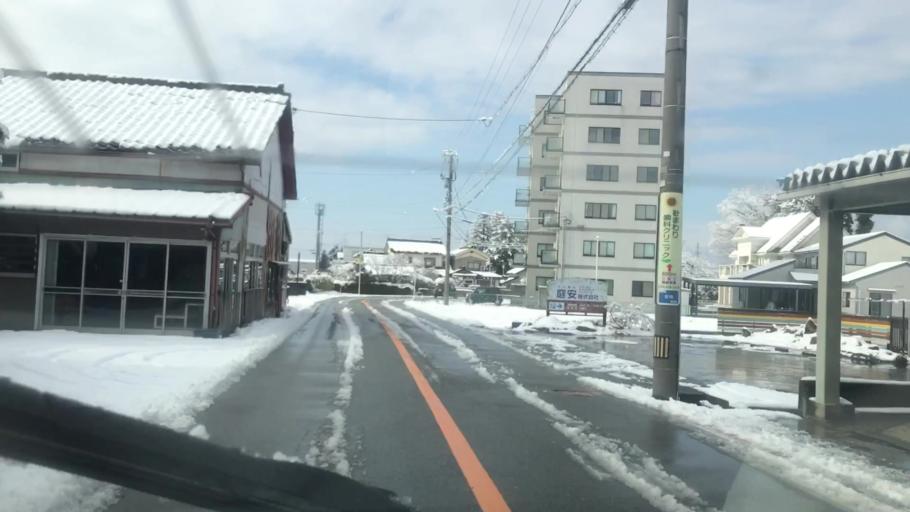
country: JP
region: Toyama
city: Toyama-shi
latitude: 36.6309
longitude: 137.2307
